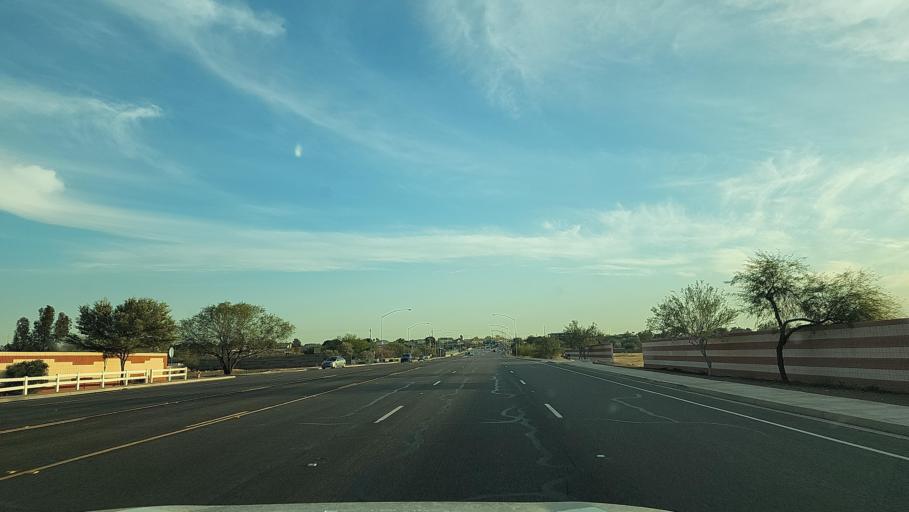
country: US
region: Arizona
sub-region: Maricopa County
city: Mesa
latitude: 33.4697
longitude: -111.7875
